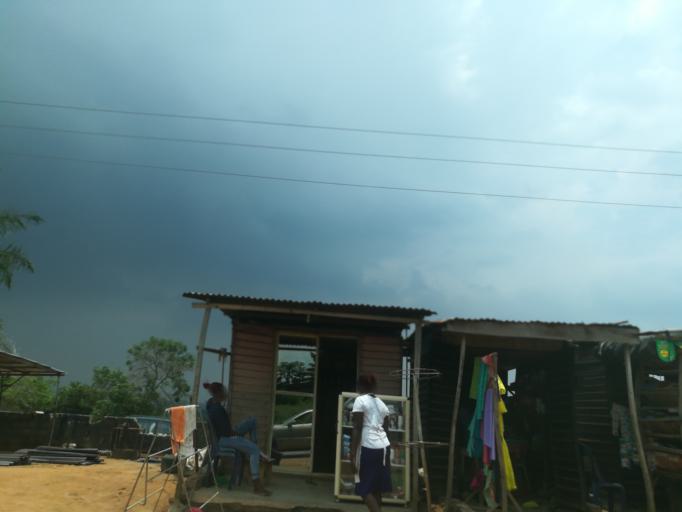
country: NG
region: Lagos
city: Ikorodu
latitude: 6.6084
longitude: 3.5839
